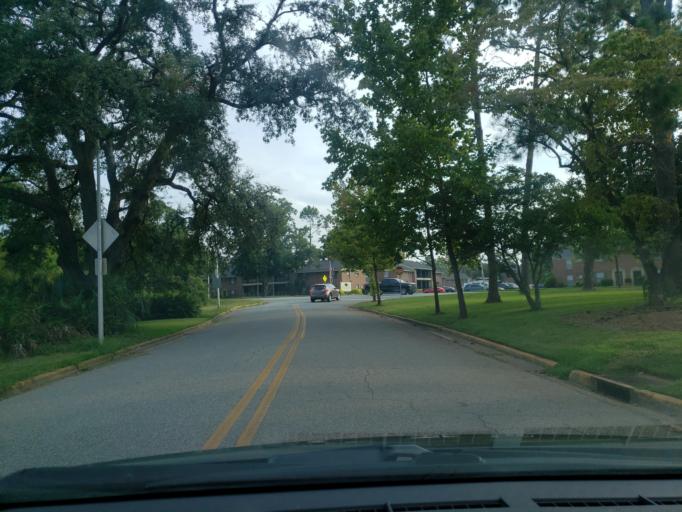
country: US
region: Georgia
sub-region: Dougherty County
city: Albany
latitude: 31.5985
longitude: -84.1998
